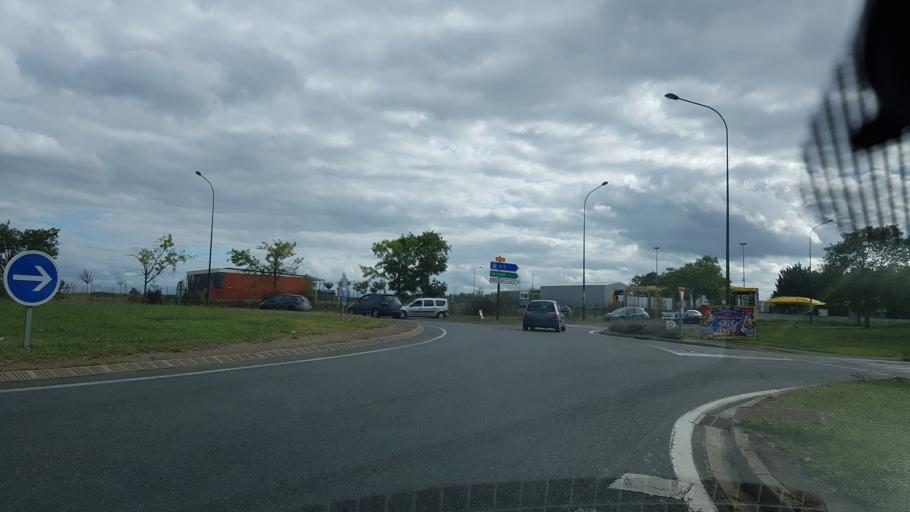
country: FR
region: Centre
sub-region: Departement du Loiret
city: Pithiviers
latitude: 48.1606
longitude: 2.2341
